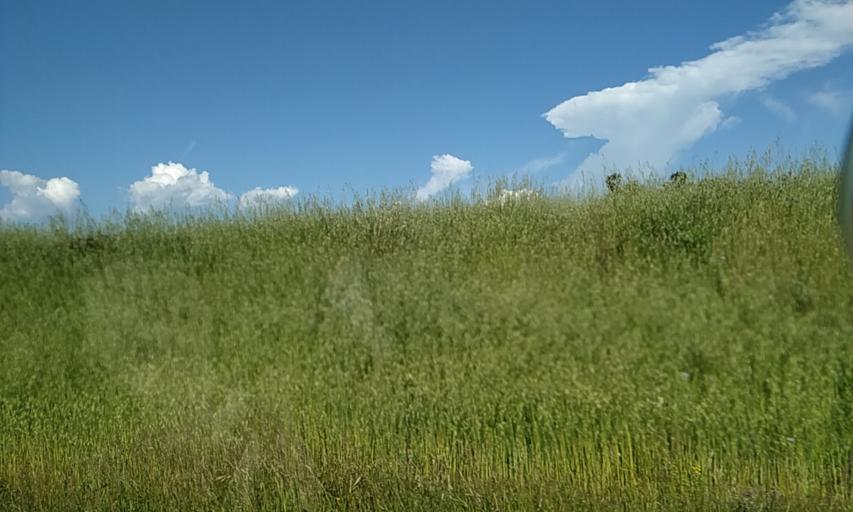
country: PT
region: Portalegre
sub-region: Portalegre
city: Urra
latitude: 39.0923
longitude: -7.4373
